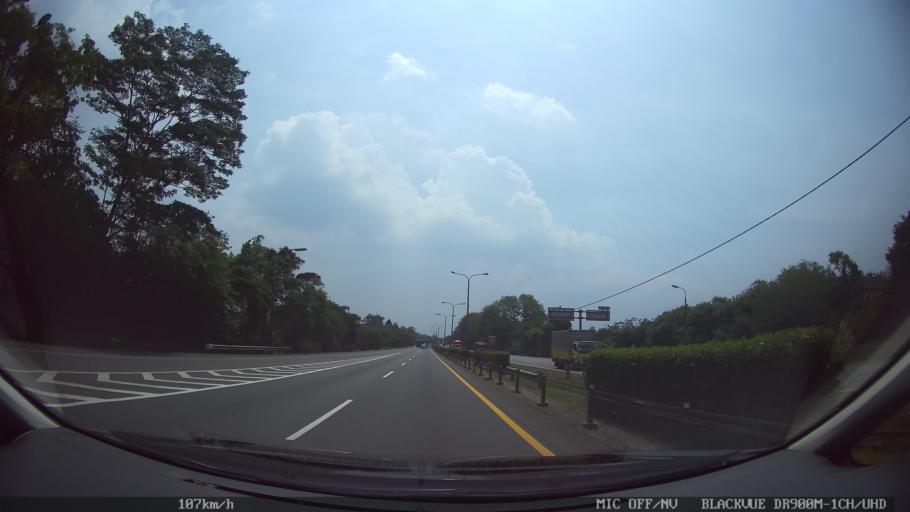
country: ID
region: Banten
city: Serang
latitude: -6.0881
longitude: 106.1443
